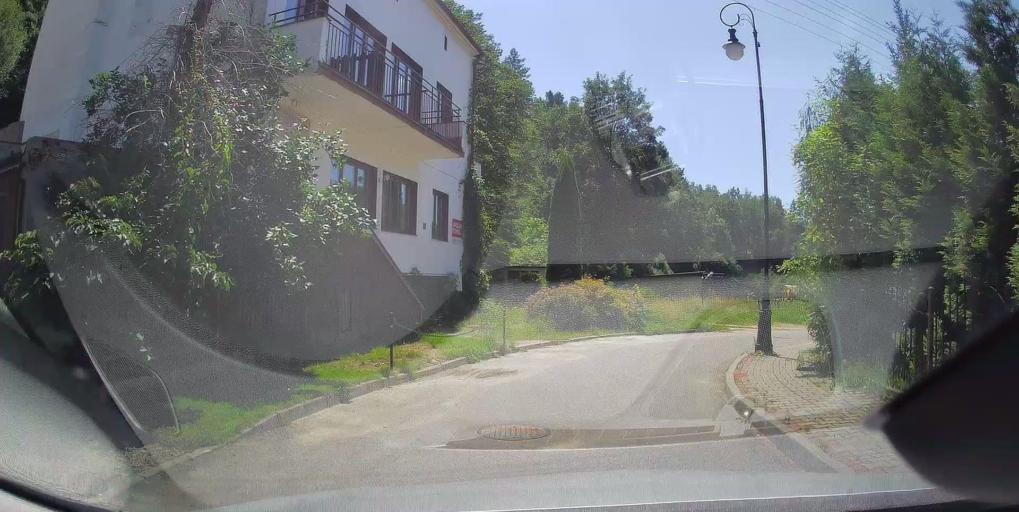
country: PL
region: Lesser Poland Voivodeship
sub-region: Powiat nowosadecki
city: Muszyna
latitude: 49.3565
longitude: 20.8904
